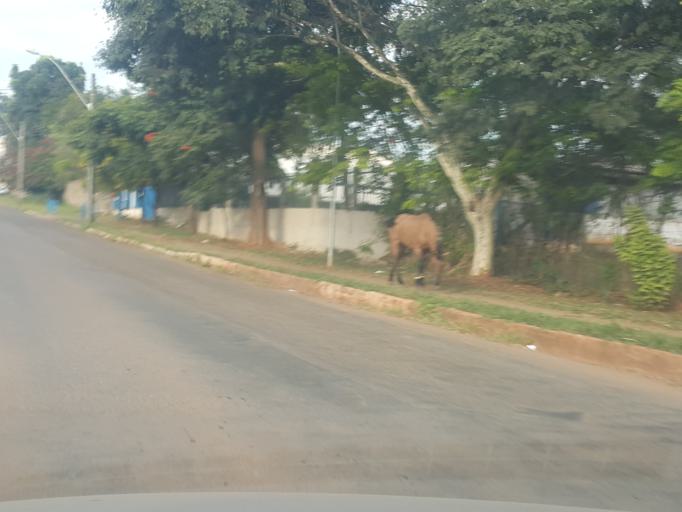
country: BR
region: Federal District
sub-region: Brasilia
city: Brasilia
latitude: -15.8251
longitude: -48.0695
